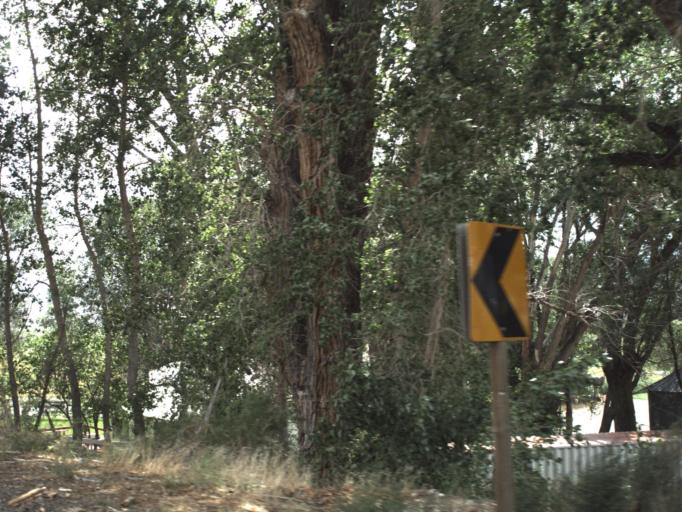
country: US
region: Utah
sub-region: Piute County
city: Junction
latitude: 38.1568
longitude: -112.0049
